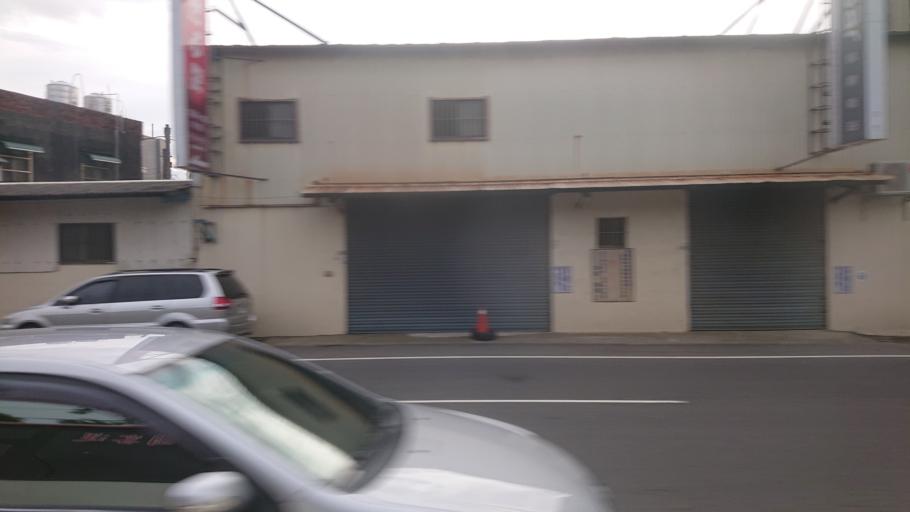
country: TW
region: Taiwan
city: Daxi
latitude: 24.8867
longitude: 121.2701
